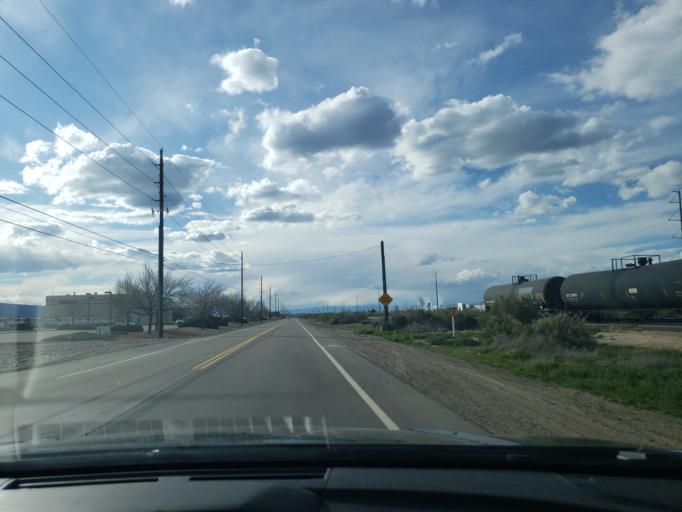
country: US
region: Colorado
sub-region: Mesa County
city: Redlands
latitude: 39.1021
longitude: -108.6308
